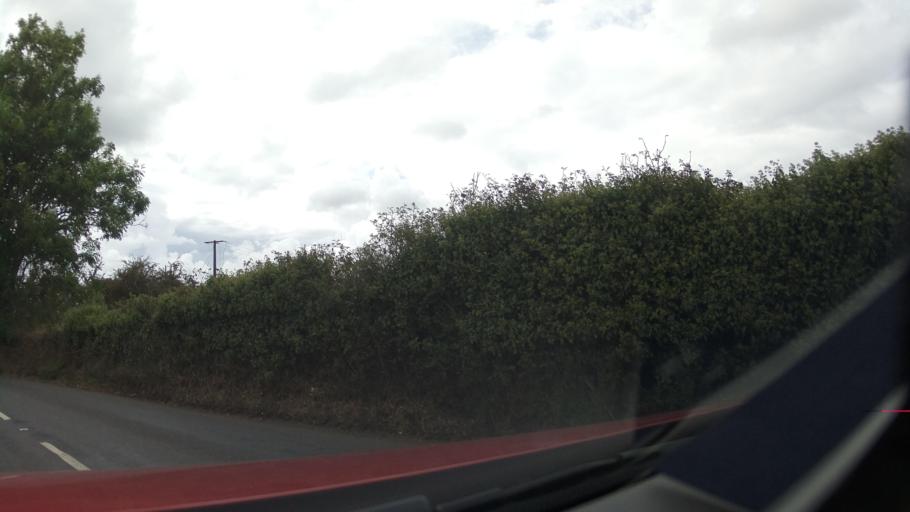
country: GB
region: England
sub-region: Telford and Wrekin
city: Newport
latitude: 52.7972
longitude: -2.3482
